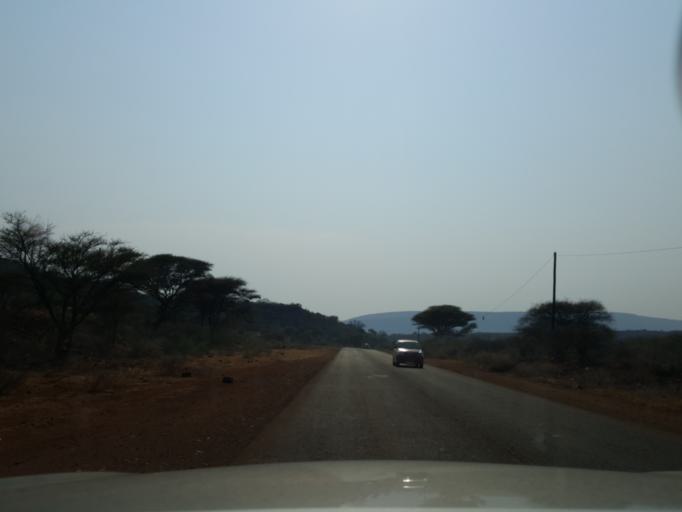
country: BW
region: South East
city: Lobatse
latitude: -25.3046
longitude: 25.8210
